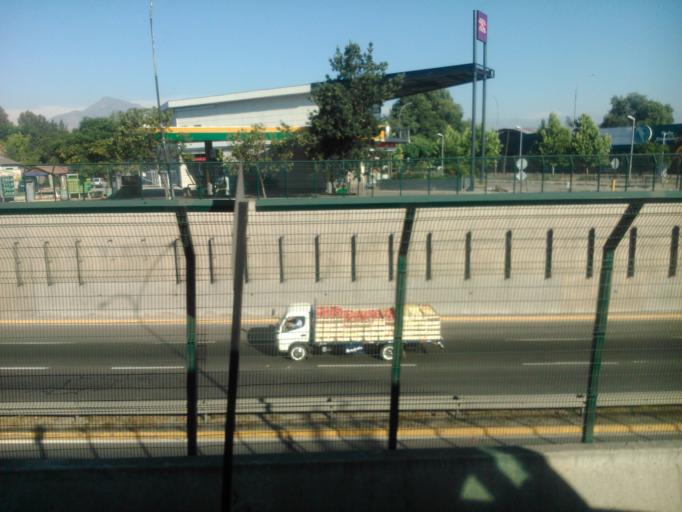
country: CL
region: Santiago Metropolitan
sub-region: Provincia de Maipo
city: Buin
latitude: -33.7328
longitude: -70.7338
